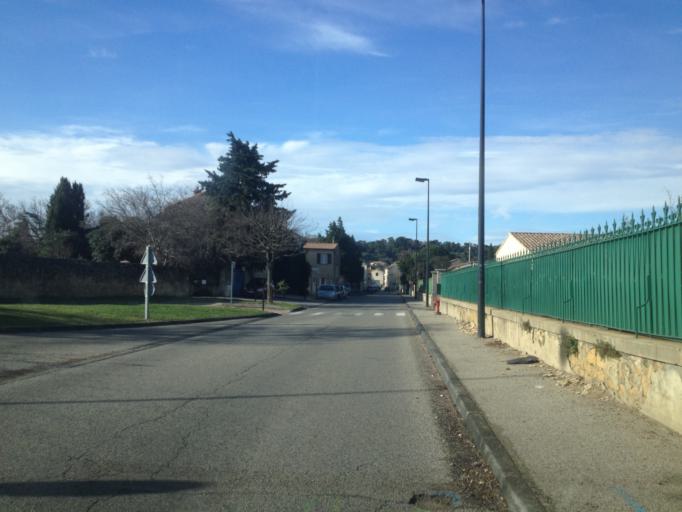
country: FR
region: Provence-Alpes-Cote d'Azur
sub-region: Departement du Vaucluse
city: Orange
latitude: 44.1298
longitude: 4.8211
